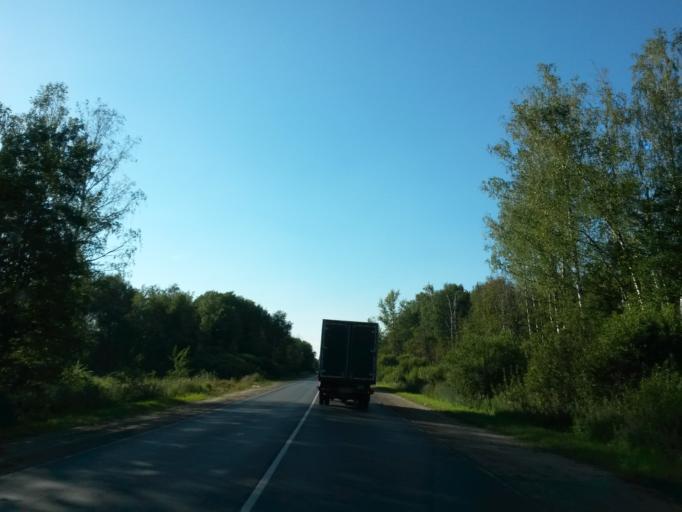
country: RU
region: Ivanovo
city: Novo-Talitsy
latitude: 57.0717
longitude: 40.6894
